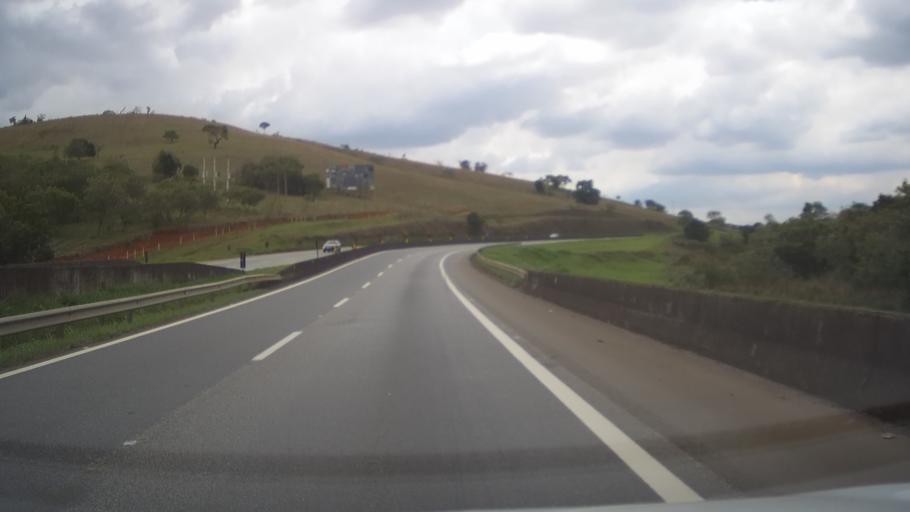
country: BR
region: Minas Gerais
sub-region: Tres Coracoes
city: Tres Coracoes
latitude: -21.5205
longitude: -45.2231
